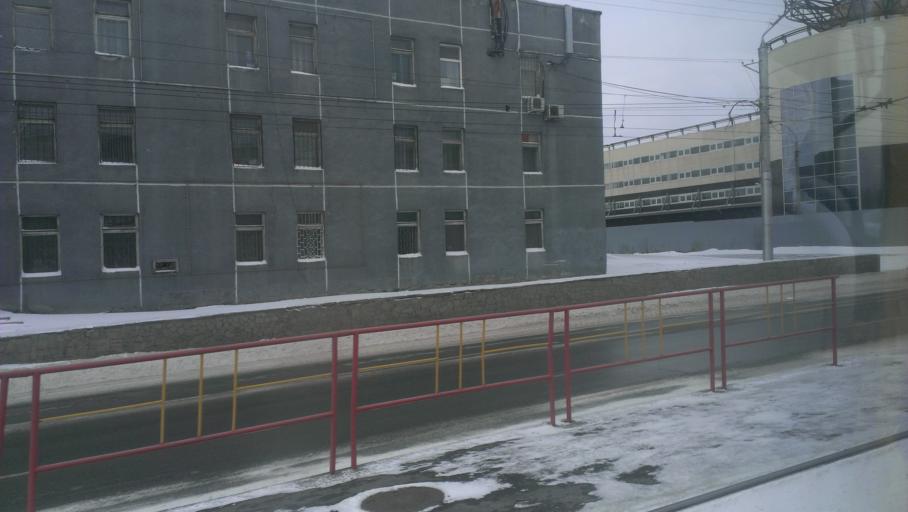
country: RU
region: Altai Krai
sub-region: Gorod Barnaulskiy
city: Barnaul
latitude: 53.3831
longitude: 83.7130
